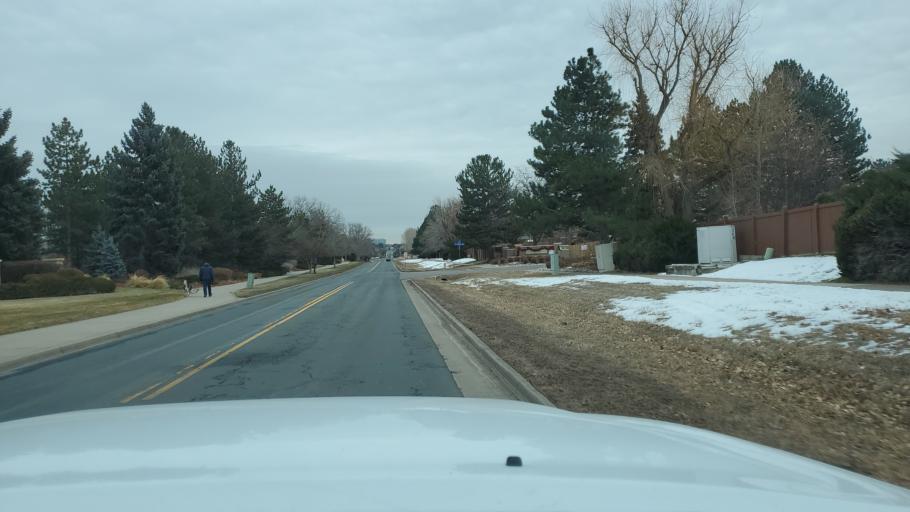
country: US
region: Colorado
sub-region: Arapahoe County
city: Greenwood Village
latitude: 39.6096
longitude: -104.9295
